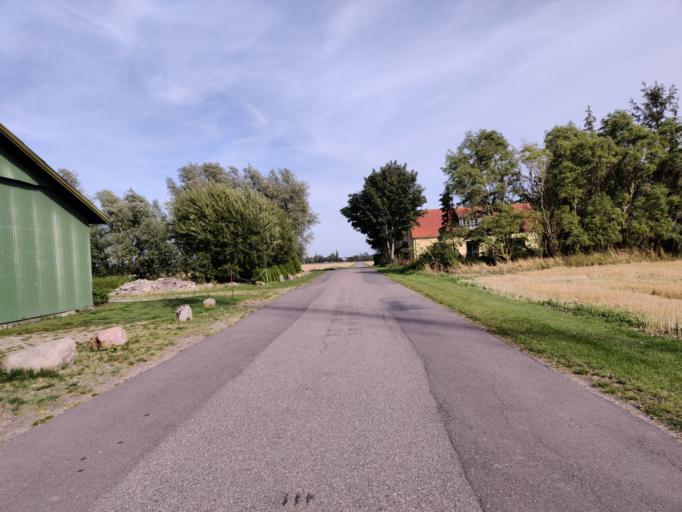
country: DK
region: Zealand
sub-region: Guldborgsund Kommune
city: Nykobing Falster
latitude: 54.6533
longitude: 11.9008
